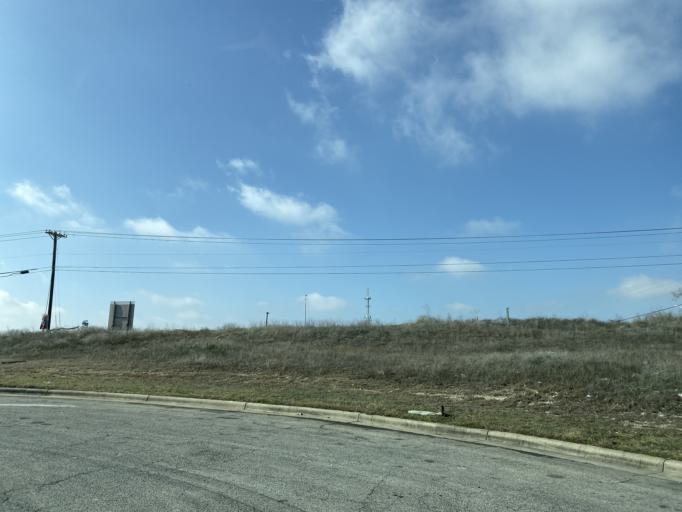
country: US
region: Texas
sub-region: Williamson County
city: Round Rock
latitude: 30.5461
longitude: -97.6912
